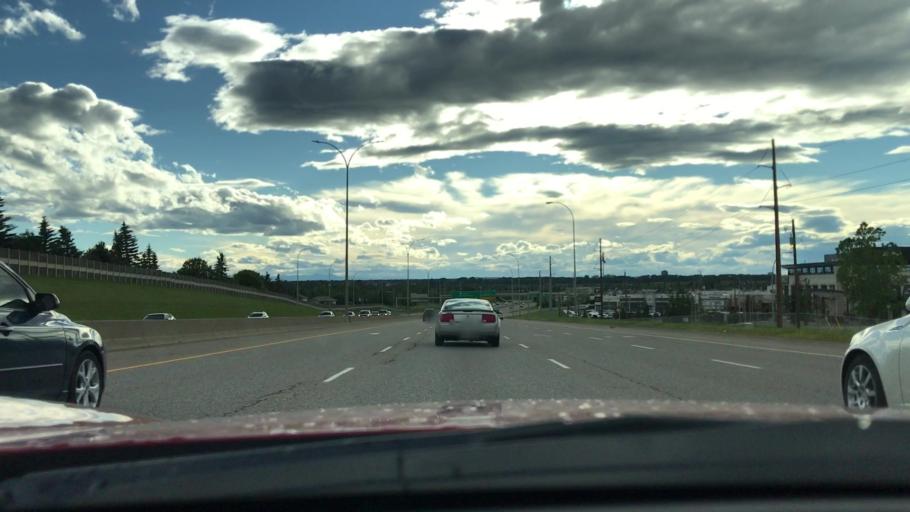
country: CA
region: Alberta
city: Calgary
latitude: 50.9472
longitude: -113.9924
